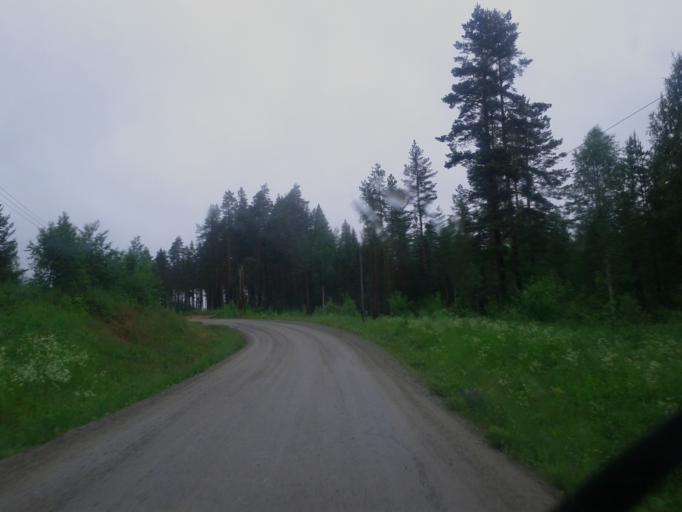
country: SE
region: Vaesternorrland
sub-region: Ange Kommun
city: Fransta
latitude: 62.3731
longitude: 16.3512
